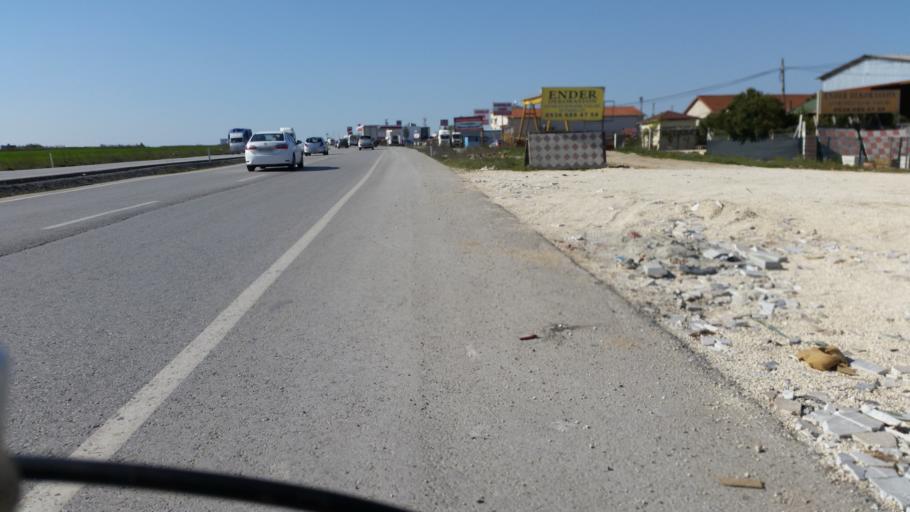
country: TR
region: Tekirdag
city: Cerkezkoey
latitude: 41.3389
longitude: 27.9664
